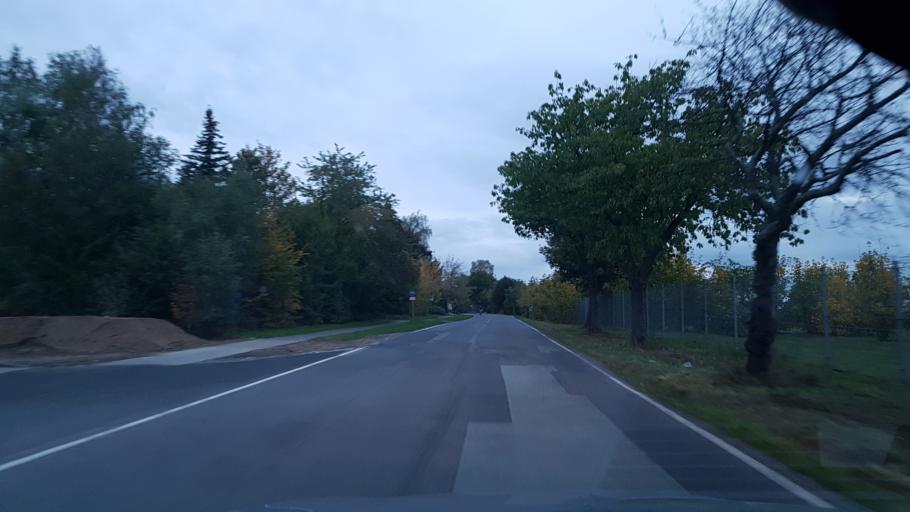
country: DE
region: Brandenburg
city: Groden
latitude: 51.4009
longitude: 13.5830
